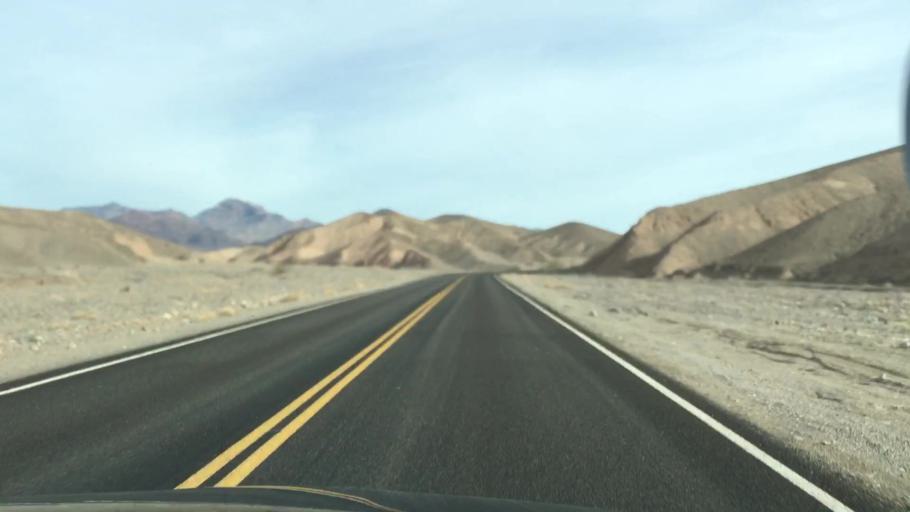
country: US
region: Nevada
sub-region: Nye County
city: Beatty
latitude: 36.6507
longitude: -117.0311
